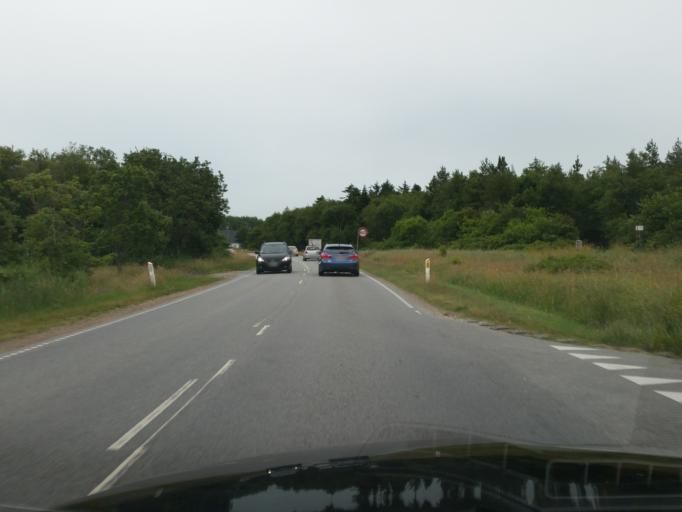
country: DK
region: South Denmark
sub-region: Varde Kommune
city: Oksbol
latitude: 55.7916
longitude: 8.2369
